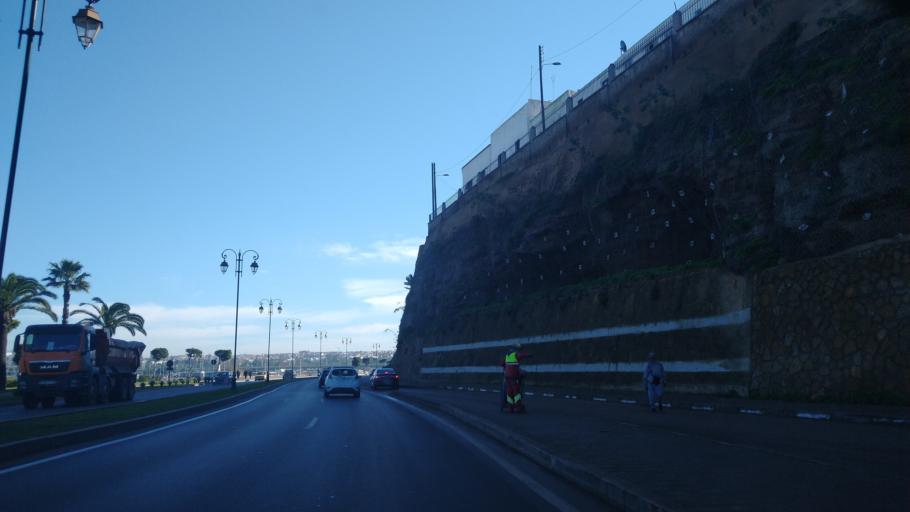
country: MA
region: Rabat-Sale-Zemmour-Zaer
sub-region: Rabat
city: Rabat
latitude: 34.0270
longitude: -6.8292
